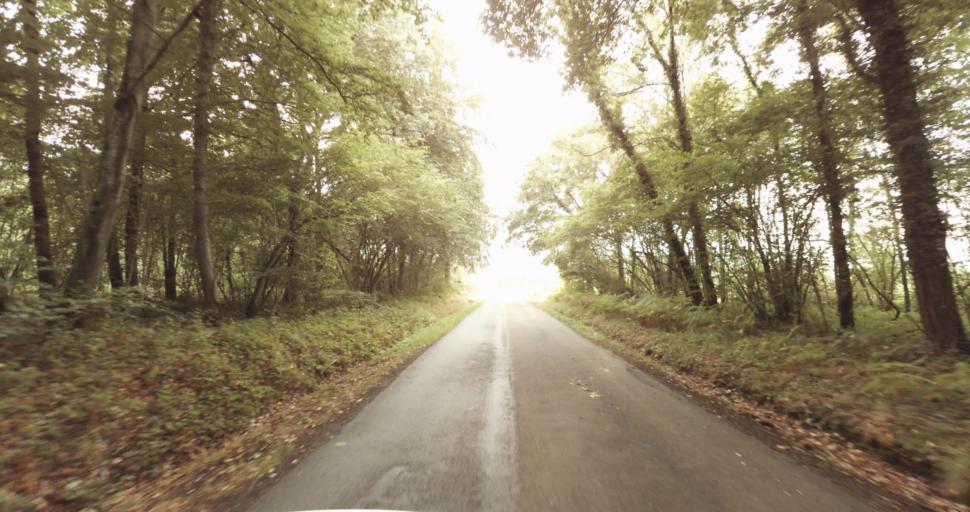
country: FR
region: Lower Normandy
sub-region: Departement de l'Orne
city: Trun
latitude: 48.9037
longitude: 0.1054
